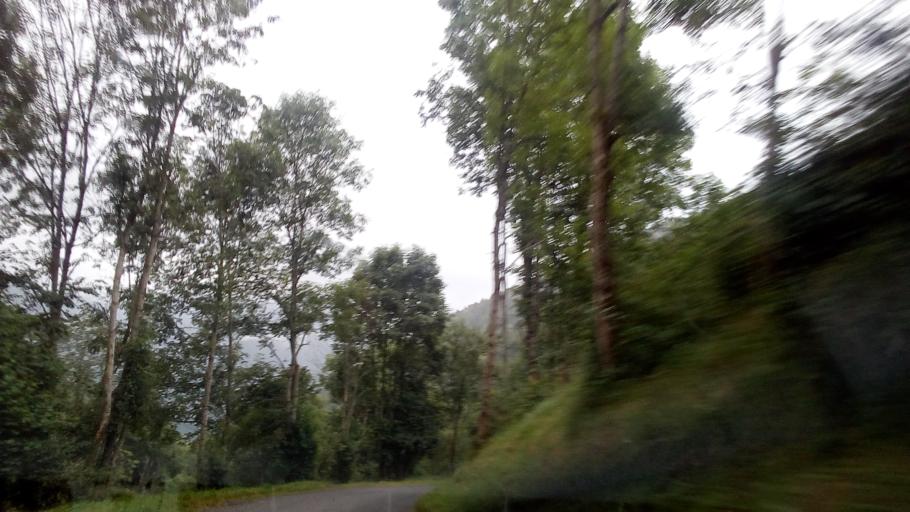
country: FR
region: Midi-Pyrenees
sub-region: Departement des Hautes-Pyrenees
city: Saint-Lary-Soulan
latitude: 42.8818
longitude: 0.3205
